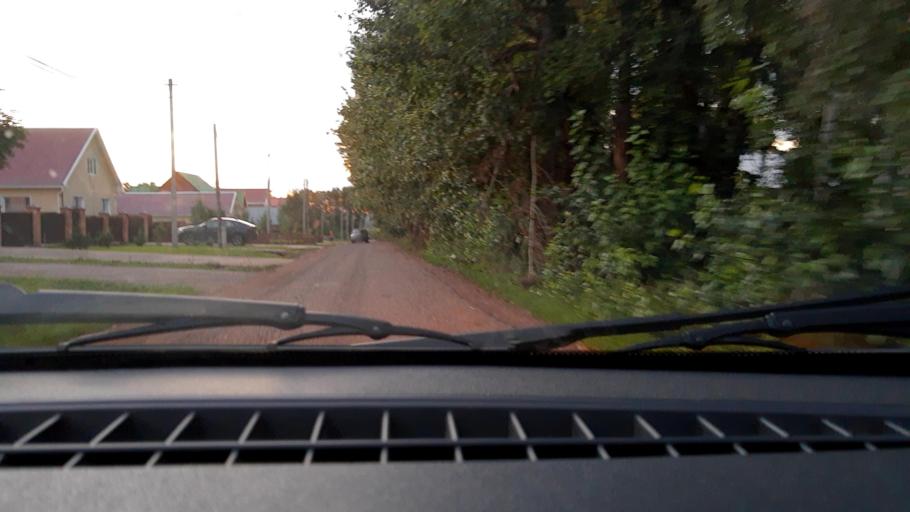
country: RU
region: Bashkortostan
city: Mikhaylovka
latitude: 54.8609
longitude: 55.8028
